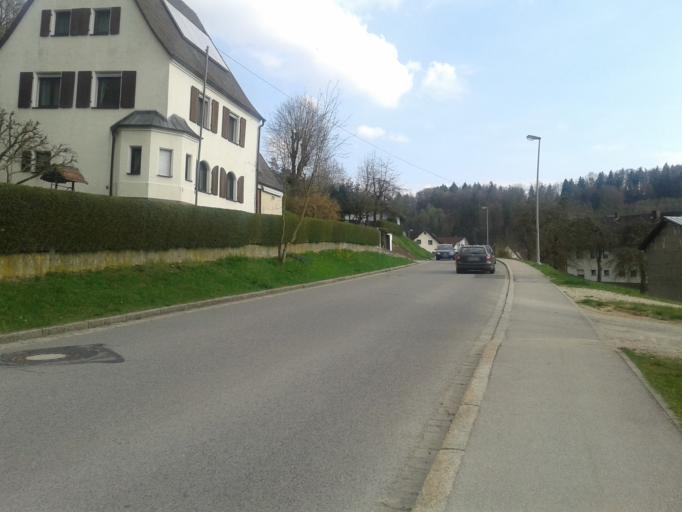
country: DE
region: Bavaria
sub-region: Upper Palatinate
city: Weigendorf
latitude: 49.5013
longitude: 11.5695
